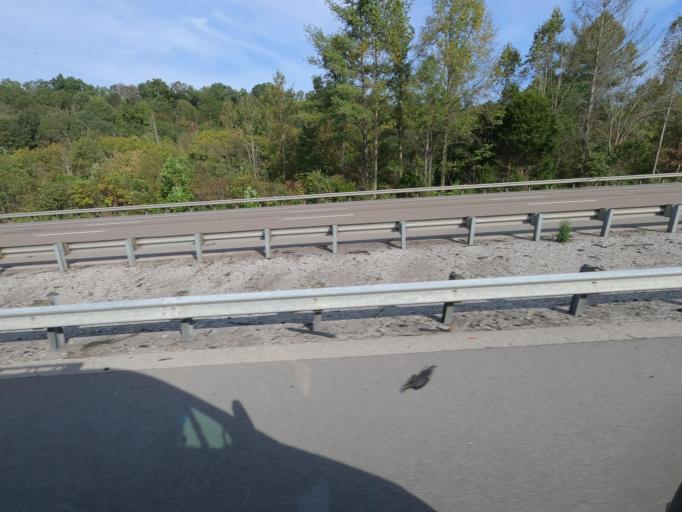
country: US
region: Tennessee
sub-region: Jefferson County
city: Dandridge
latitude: 36.0188
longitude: -83.4909
